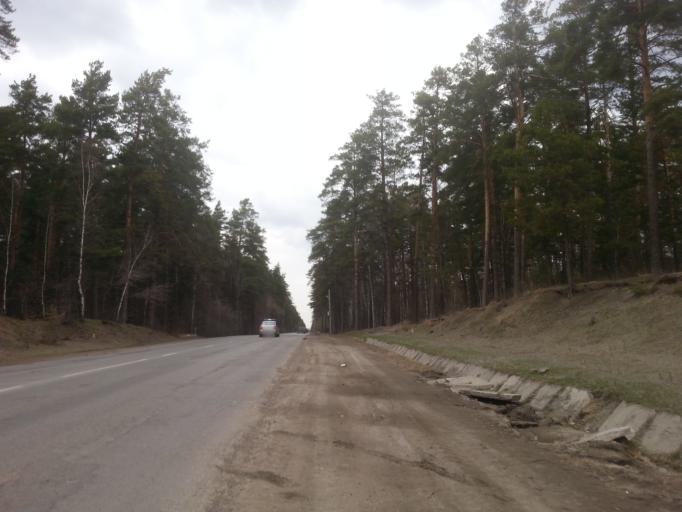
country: RU
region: Altai Krai
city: Yuzhnyy
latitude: 53.2713
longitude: 83.7241
